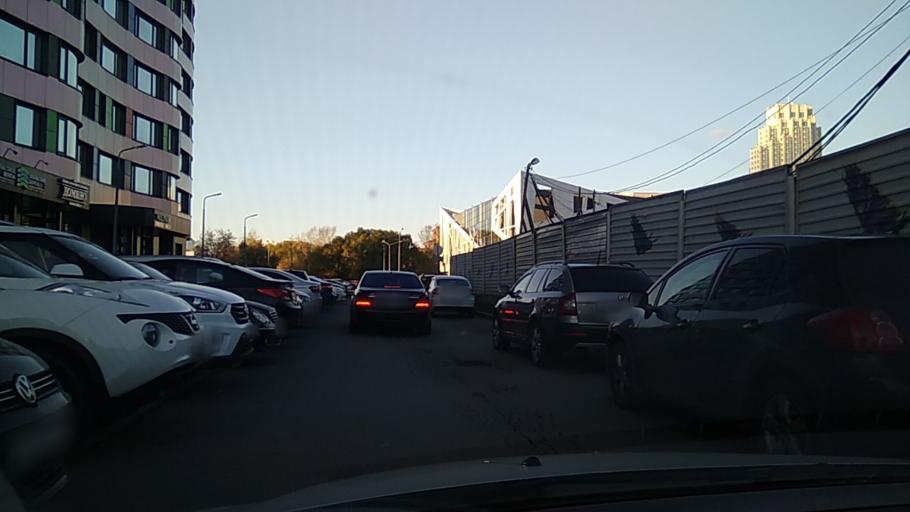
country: RU
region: Sverdlovsk
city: Yekaterinburg
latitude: 56.8245
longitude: 60.6071
